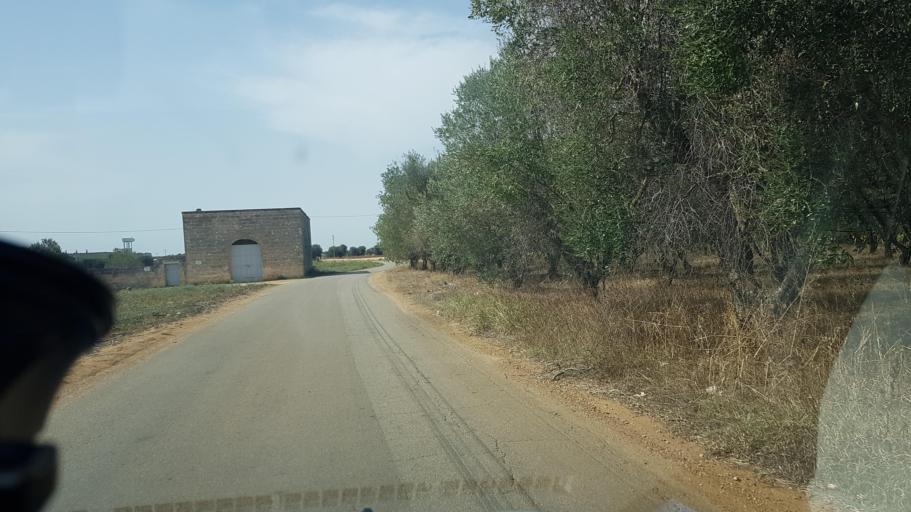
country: IT
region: Apulia
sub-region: Provincia di Brindisi
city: Mesagne
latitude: 40.5739
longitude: 17.8379
